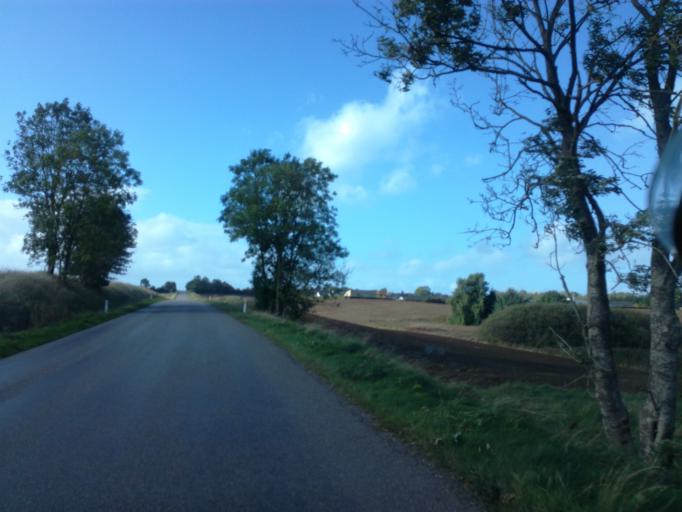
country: DK
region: South Denmark
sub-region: Vejle Kommune
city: Brejning
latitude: 55.6318
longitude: 9.7089
